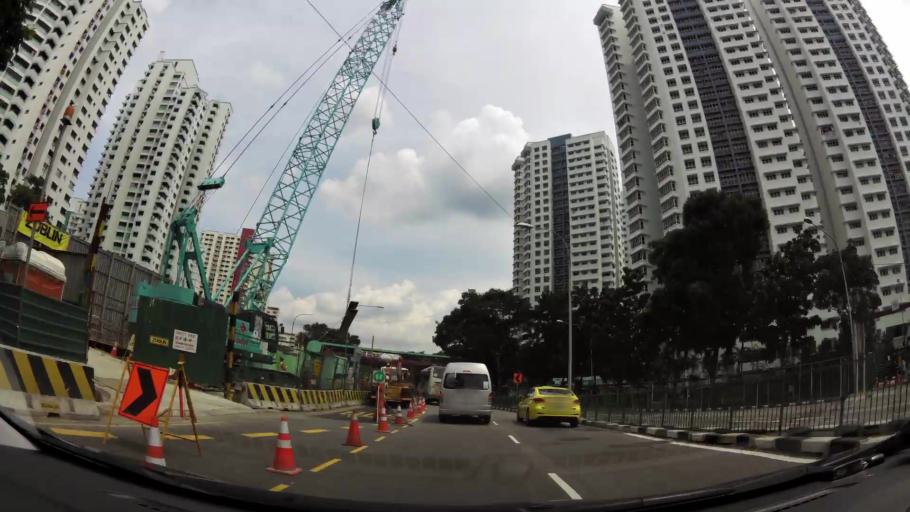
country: MY
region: Johor
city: Johor Bahru
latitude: 1.3800
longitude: 103.7617
